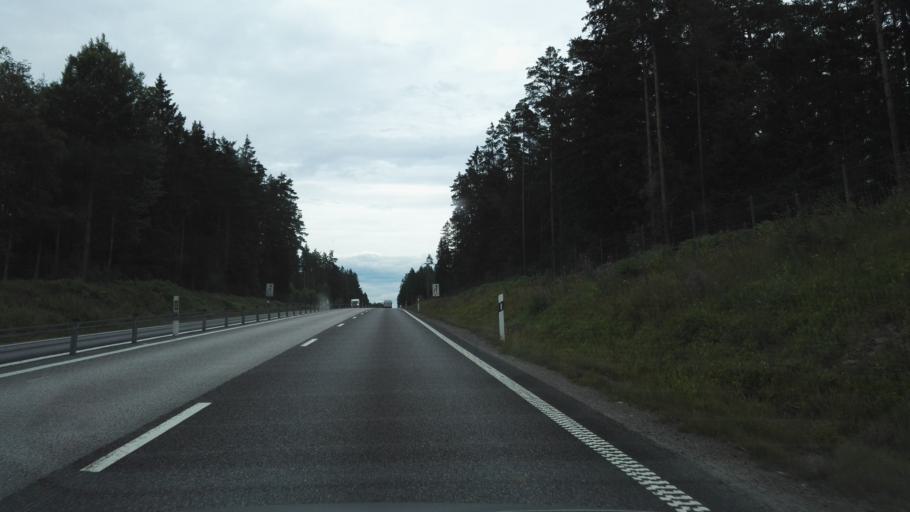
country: SE
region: Kronoberg
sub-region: Vaxjo Kommun
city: Rottne
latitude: 56.9548
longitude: 14.9365
